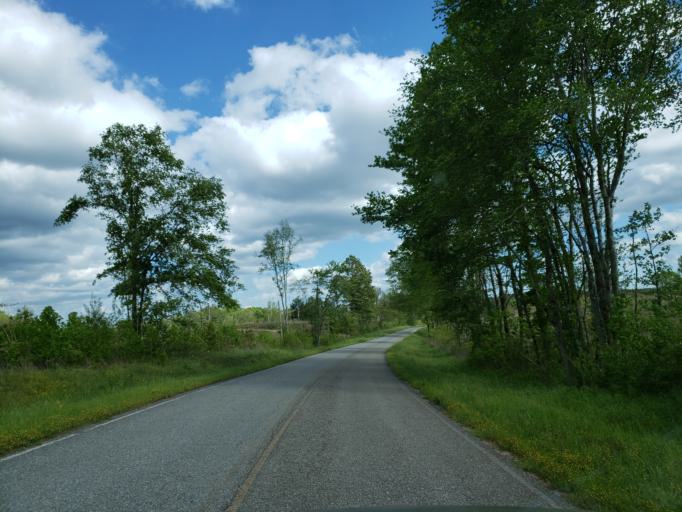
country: US
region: Georgia
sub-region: Haralson County
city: Tallapoosa
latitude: 33.7170
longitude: -85.3866
